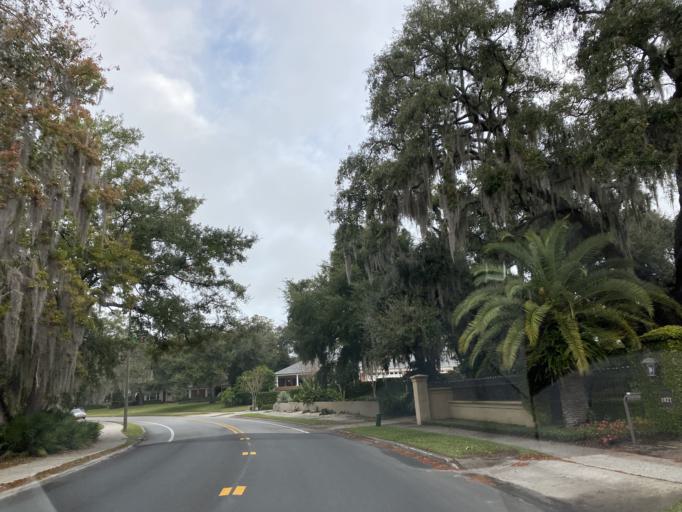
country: US
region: Florida
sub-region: Orange County
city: Orlando
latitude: 28.5588
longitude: -81.3881
